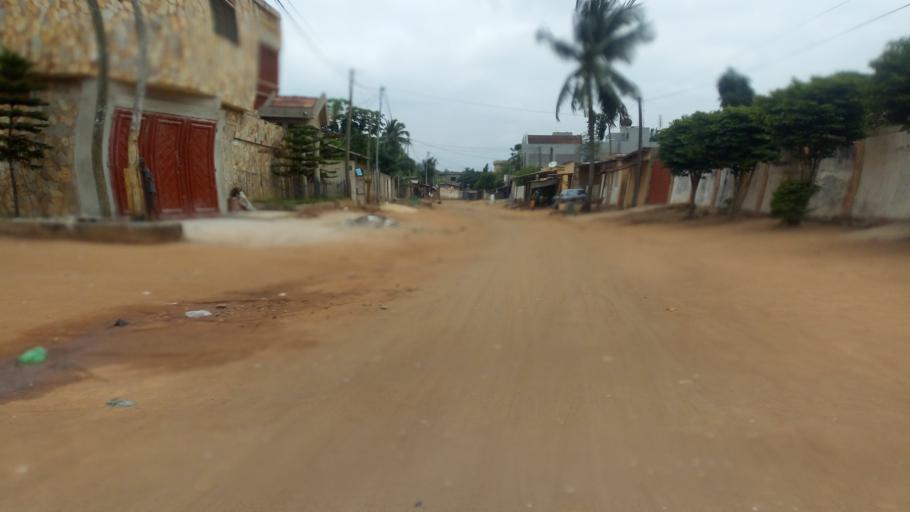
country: TG
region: Maritime
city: Lome
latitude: 6.1862
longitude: 1.1859
